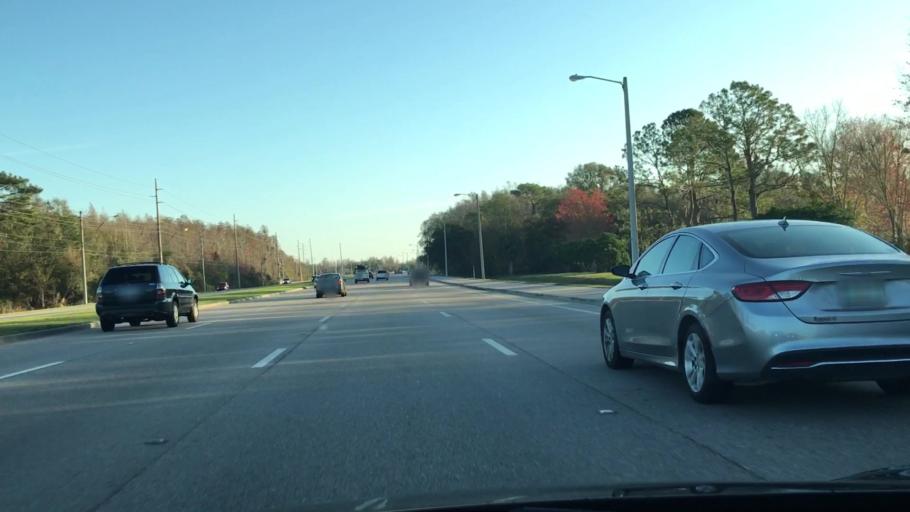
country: US
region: Florida
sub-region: Hillsborough County
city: Pebble Creek
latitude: 28.1389
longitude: -82.3585
